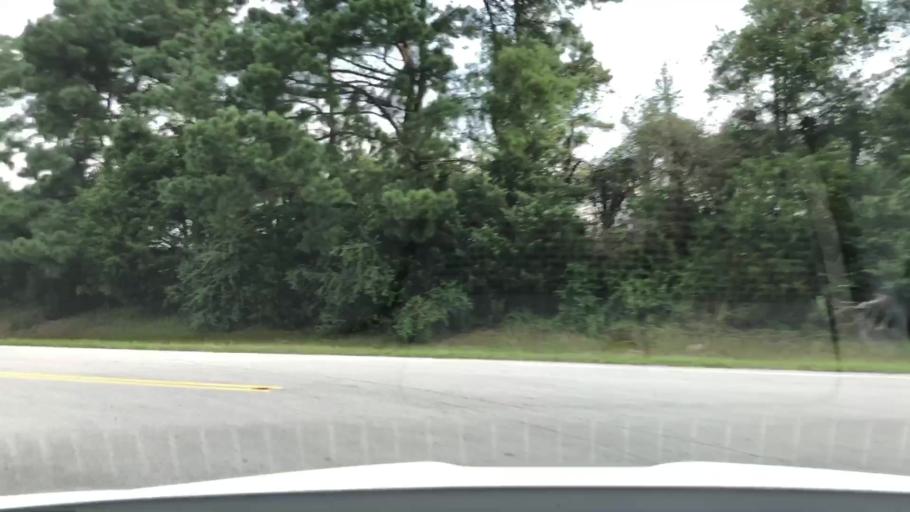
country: US
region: North Carolina
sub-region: Jones County
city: Trenton
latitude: 35.0011
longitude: -77.2736
